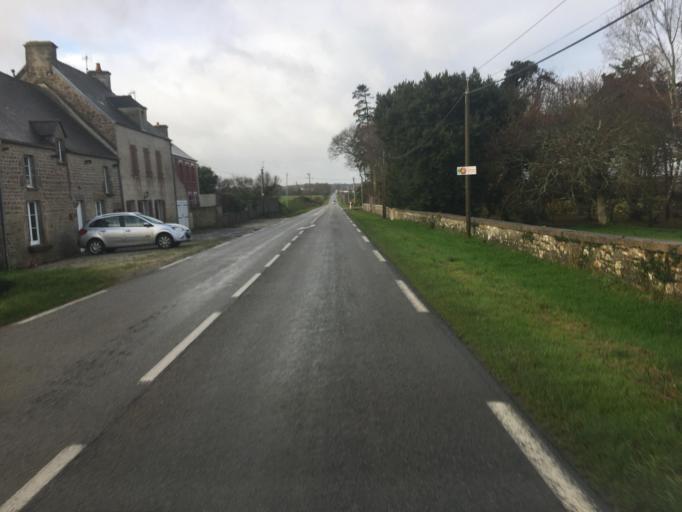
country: FR
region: Lower Normandy
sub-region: Departement de la Manche
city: Saint-Pierre-Eglise
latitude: 49.6682
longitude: -1.3784
